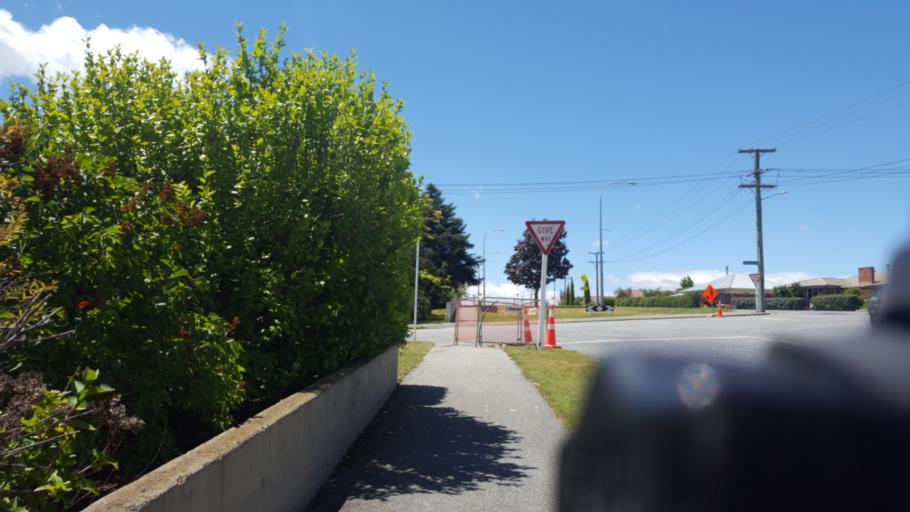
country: NZ
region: Otago
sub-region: Queenstown-Lakes District
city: Wanaka
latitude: -45.2504
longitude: 169.3957
